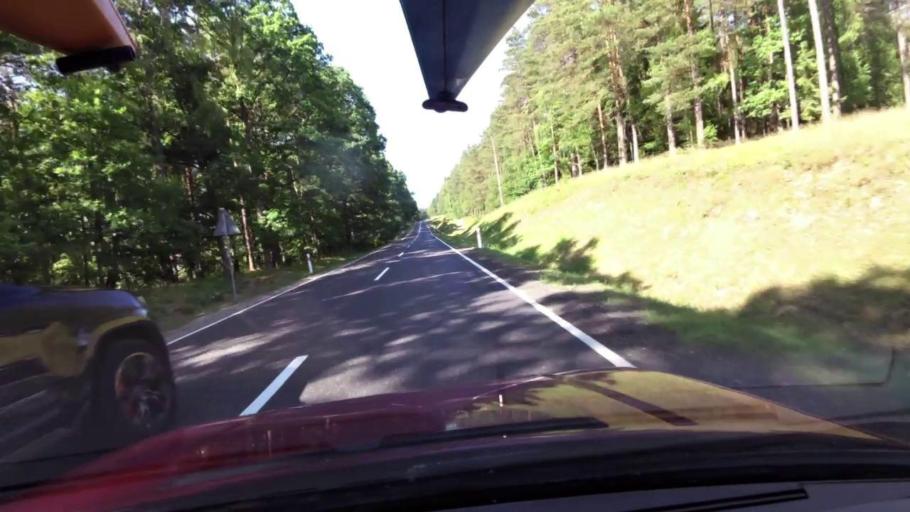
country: PL
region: Pomeranian Voivodeship
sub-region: Powiat bytowski
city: Trzebielino
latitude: 54.1201
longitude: 17.0029
